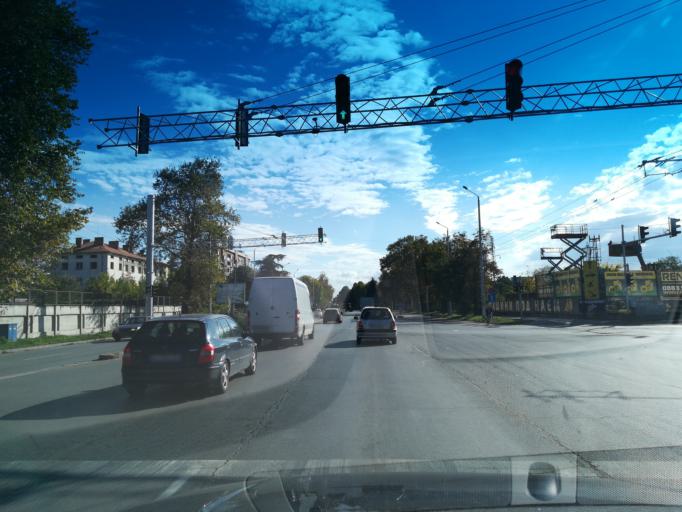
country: BG
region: Stara Zagora
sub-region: Obshtina Stara Zagora
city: Stara Zagora
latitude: 42.4100
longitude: 25.6397
